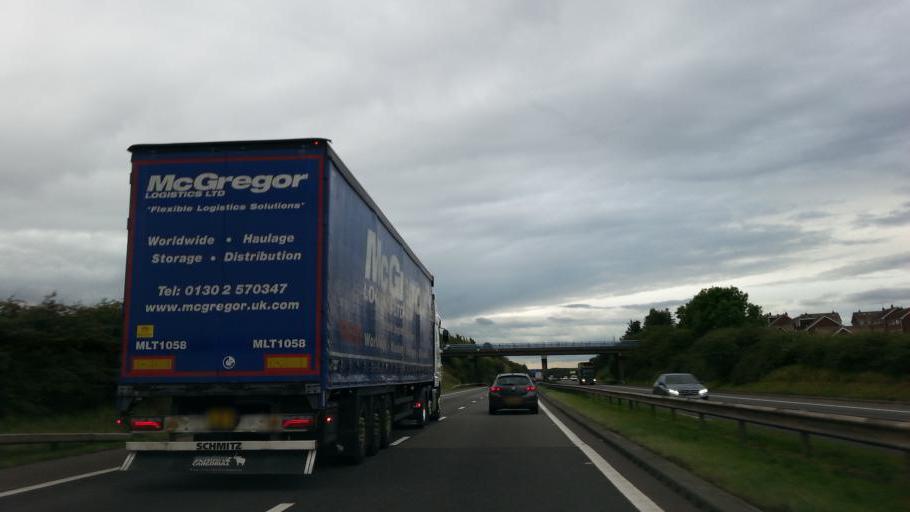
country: GB
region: England
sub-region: Doncaster
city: Tickhill
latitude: 53.4105
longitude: -1.0823
